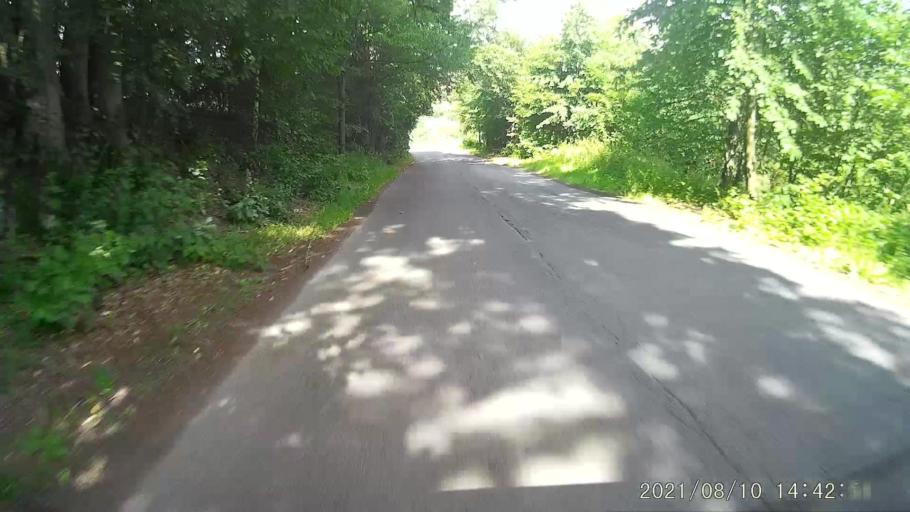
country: PL
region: Lower Silesian Voivodeship
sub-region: Powiat klodzki
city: Radkow
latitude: 50.5503
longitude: 16.4328
